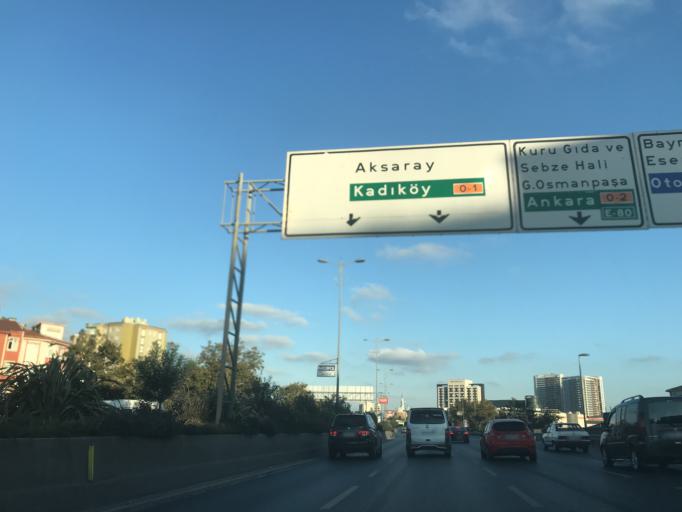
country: TR
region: Istanbul
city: Esenler
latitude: 41.0467
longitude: 28.8796
